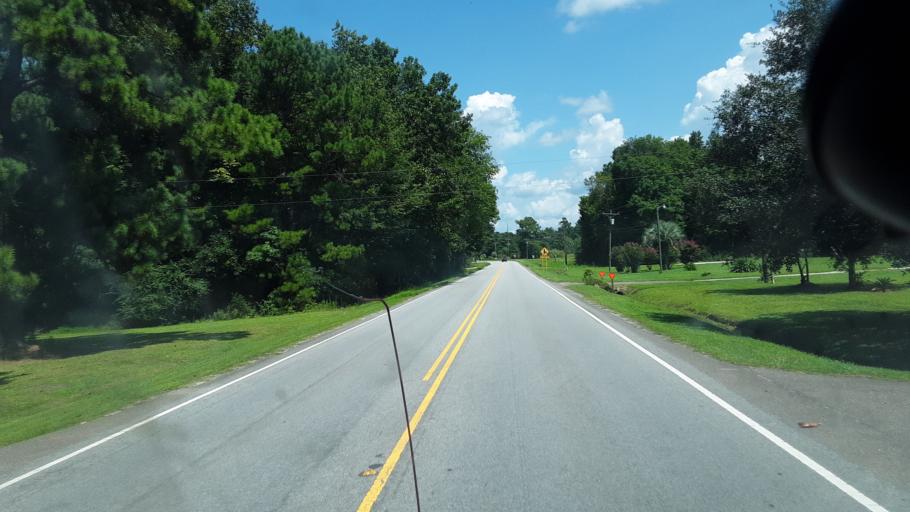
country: US
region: South Carolina
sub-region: Berkeley County
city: Moncks Corner
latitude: 33.2370
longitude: -79.9447
